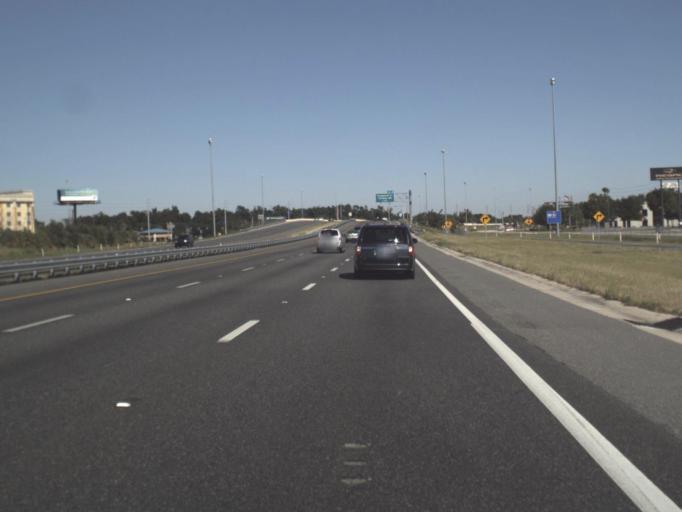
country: US
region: Florida
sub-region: Orange County
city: Belle Isle
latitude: 28.4480
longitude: -81.3555
